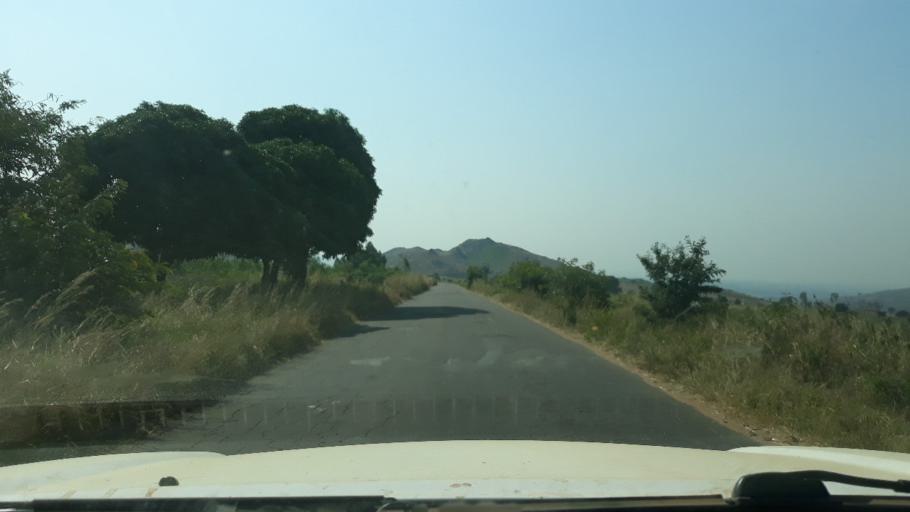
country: BI
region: Cibitoke
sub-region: Commune of Buganda
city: Buganda
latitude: -3.1076
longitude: 29.1379
